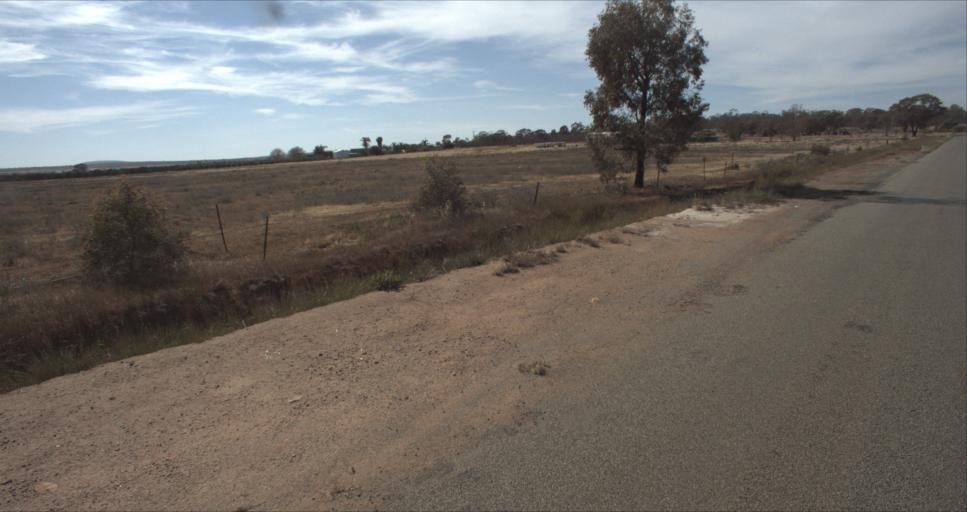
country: AU
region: New South Wales
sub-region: Leeton
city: Leeton
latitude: -34.5756
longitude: 146.4768
